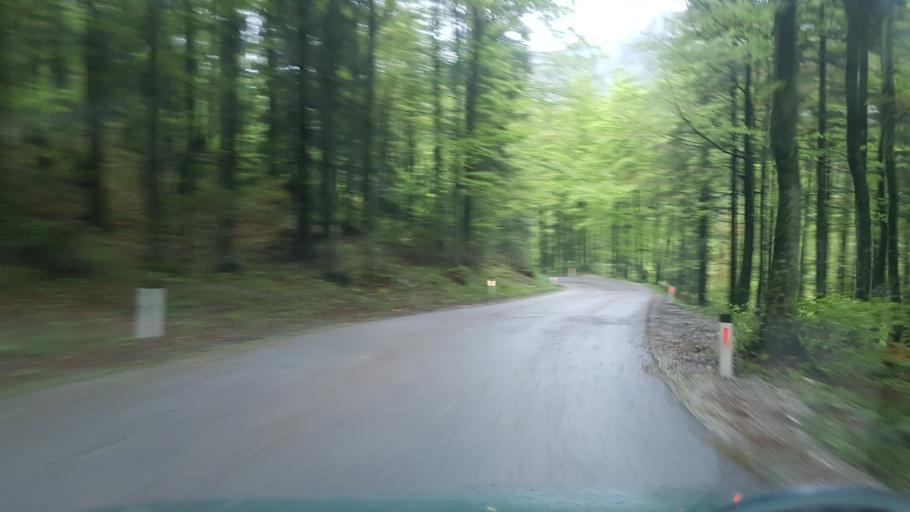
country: SI
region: Bohinj
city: Bohinjska Bistrica
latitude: 46.2289
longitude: 14.0235
